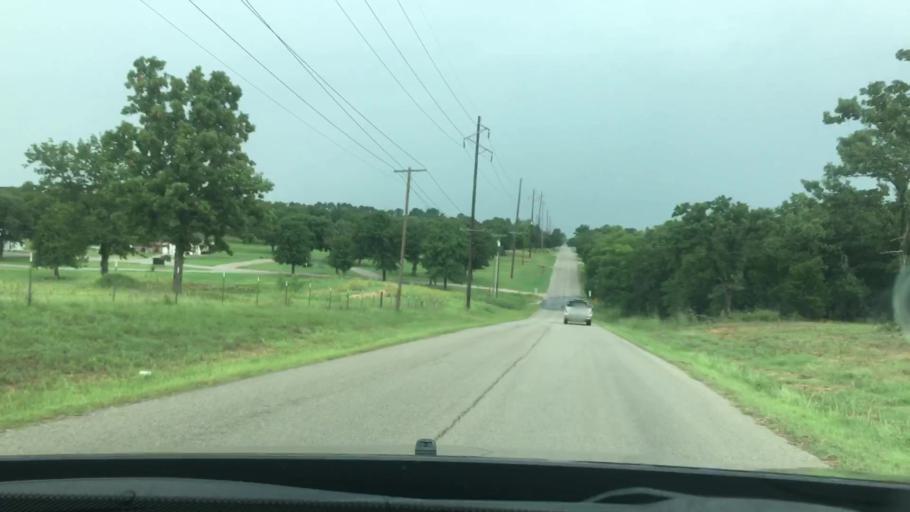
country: US
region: Oklahoma
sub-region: Carter County
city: Healdton
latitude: 34.2168
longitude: -97.4922
